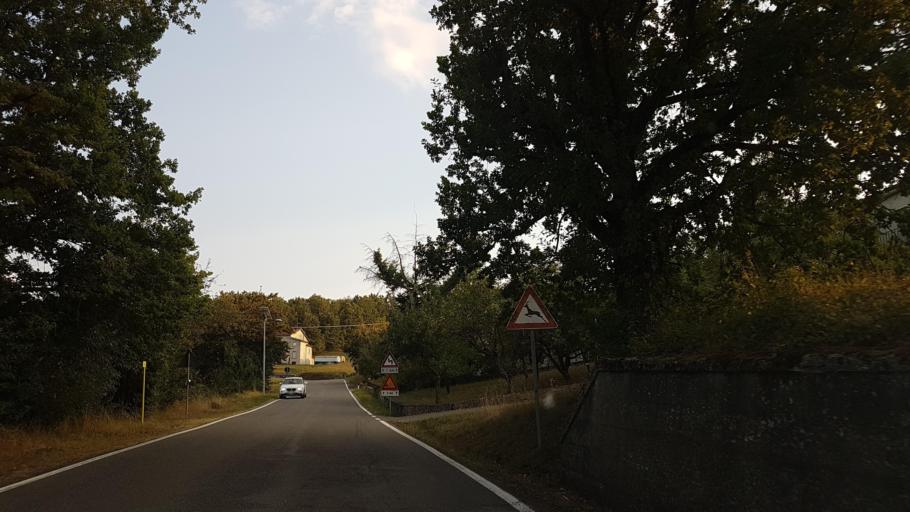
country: IT
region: Emilia-Romagna
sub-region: Provincia di Parma
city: Albareto
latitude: 44.4764
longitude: 9.7112
